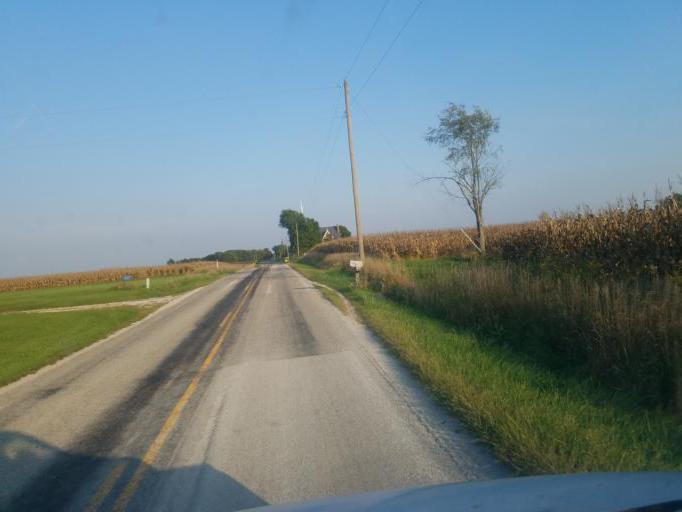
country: US
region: Ohio
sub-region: Crawford County
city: Bucyrus
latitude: 40.8964
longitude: -82.8903
